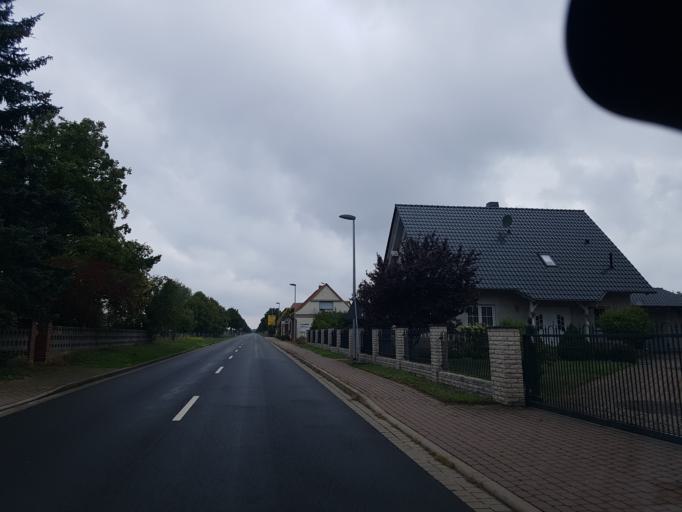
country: DE
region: Saxony-Anhalt
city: Tucheim
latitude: 52.3058
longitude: 12.0890
